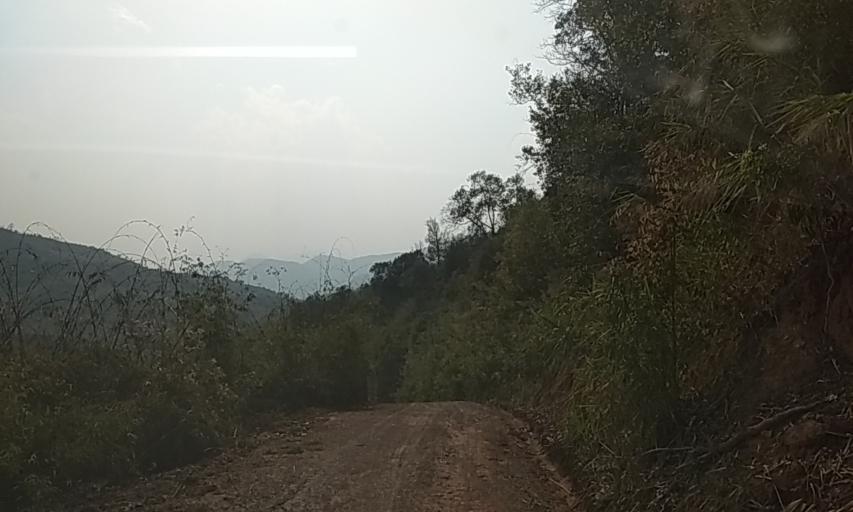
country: LA
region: Louangphabang
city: Louangphabang
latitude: 20.0398
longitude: 101.8178
